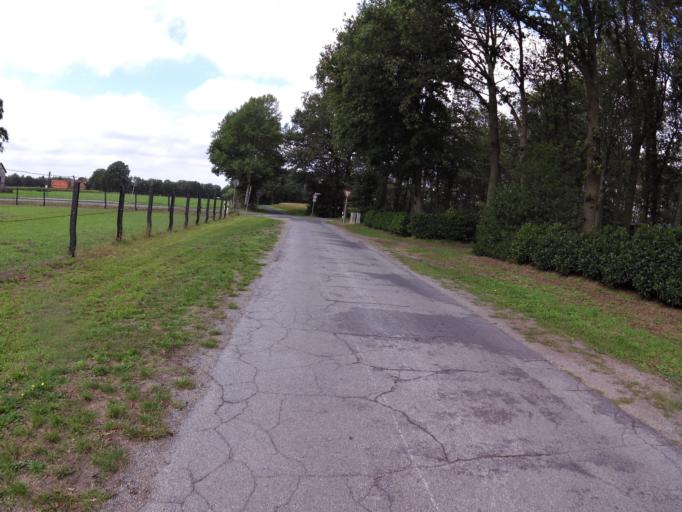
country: DE
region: North Rhine-Westphalia
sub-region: Regierungsbezirk Munster
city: Gronau
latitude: 52.1566
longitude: 7.0235
